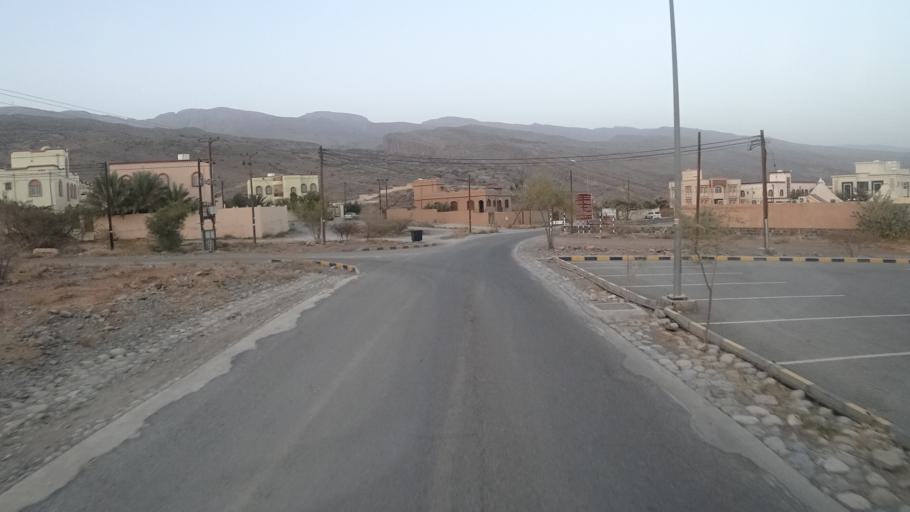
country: OM
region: Muhafazat ad Dakhiliyah
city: Bahla'
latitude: 23.1376
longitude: 57.3058
